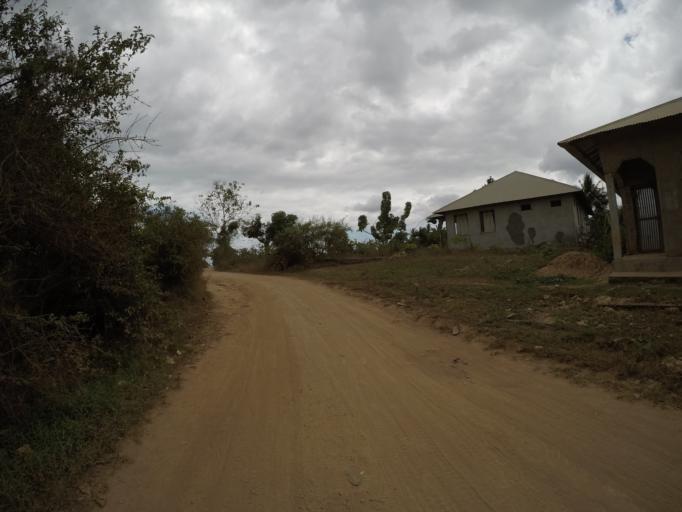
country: TZ
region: Zanzibar Central/South
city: Koani
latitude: -6.1937
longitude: 39.3044
